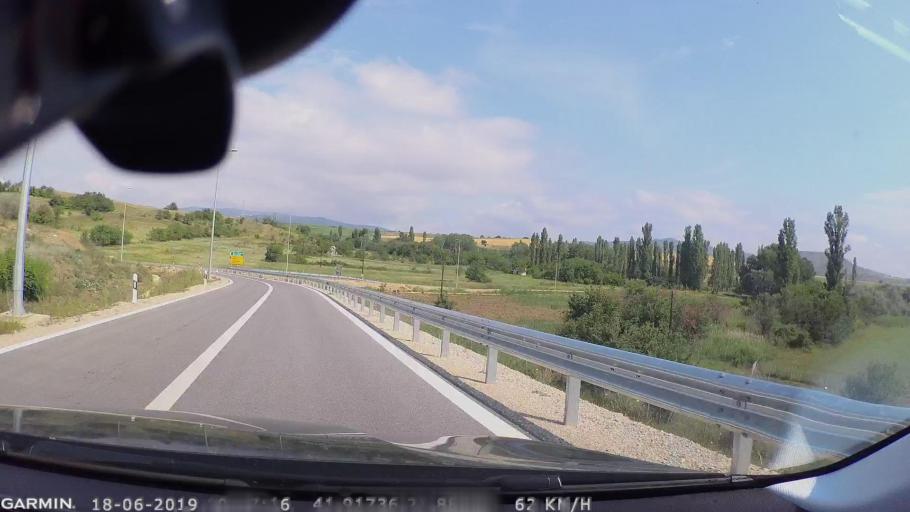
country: MK
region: Sveti Nikole
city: Gorobinci
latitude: 41.9148
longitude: 21.8849
